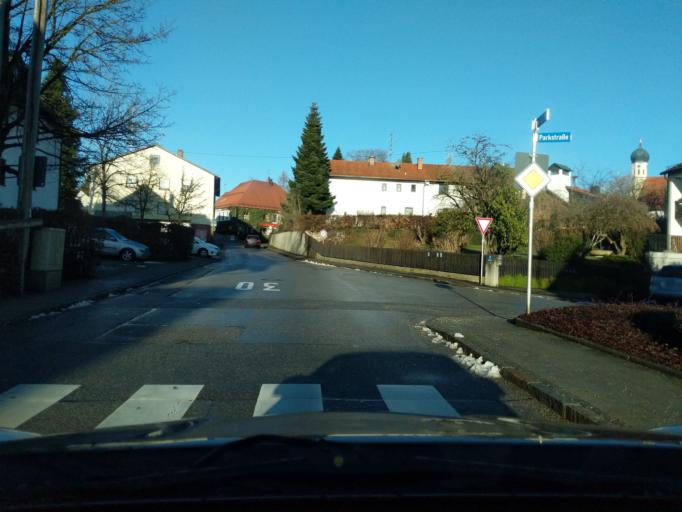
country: DE
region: Bavaria
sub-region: Upper Bavaria
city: Zorneding
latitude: 48.0941
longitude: 11.8346
